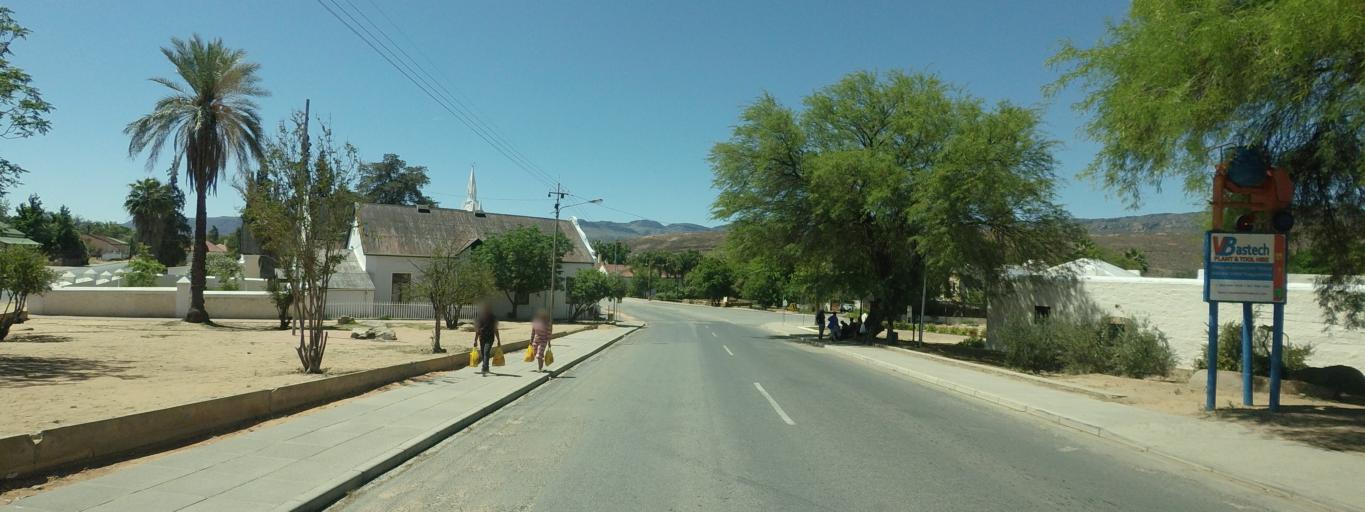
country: ZA
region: Western Cape
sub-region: West Coast District Municipality
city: Clanwilliam
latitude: -32.1813
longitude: 18.8934
